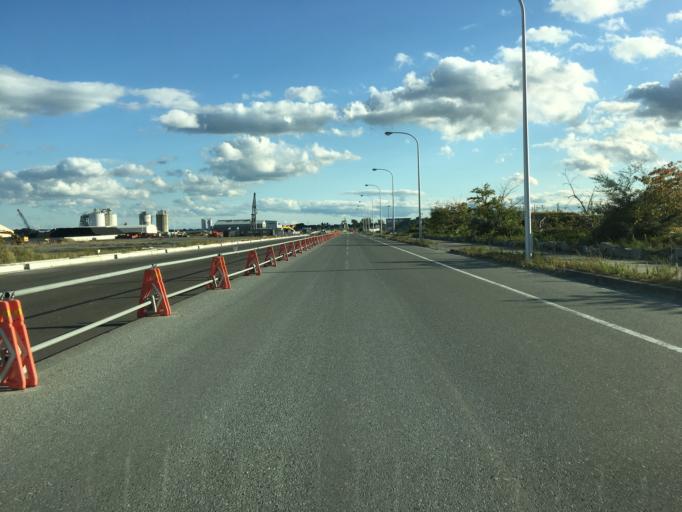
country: JP
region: Miyagi
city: Marumori
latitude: 37.8423
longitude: 140.9511
